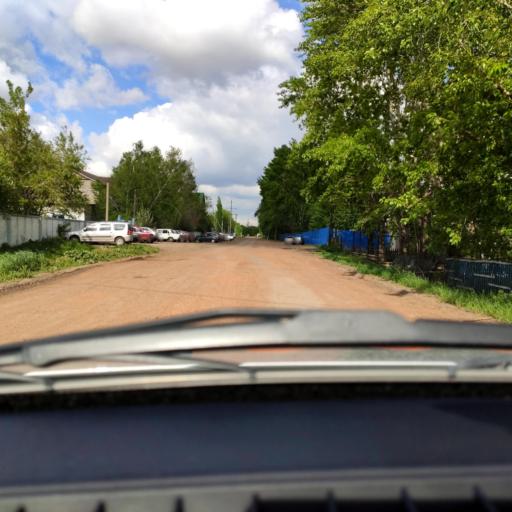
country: RU
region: Bashkortostan
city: Tolbazy
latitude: 54.0046
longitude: 55.8986
